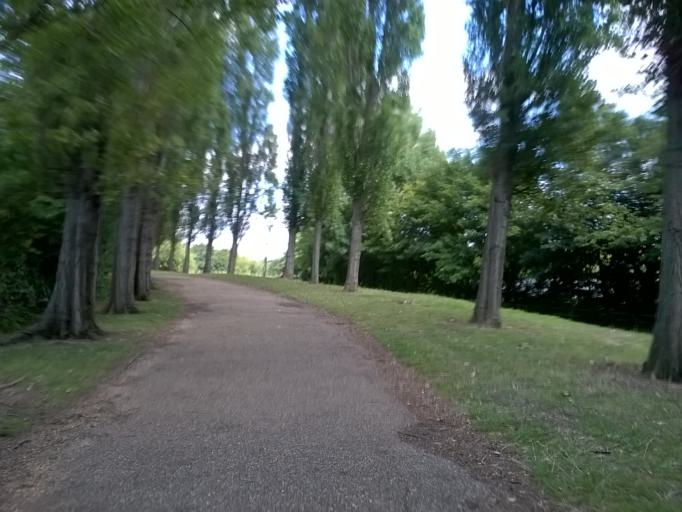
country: GB
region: England
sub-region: Milton Keynes
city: Milton Keynes
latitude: 52.0570
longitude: -0.7318
